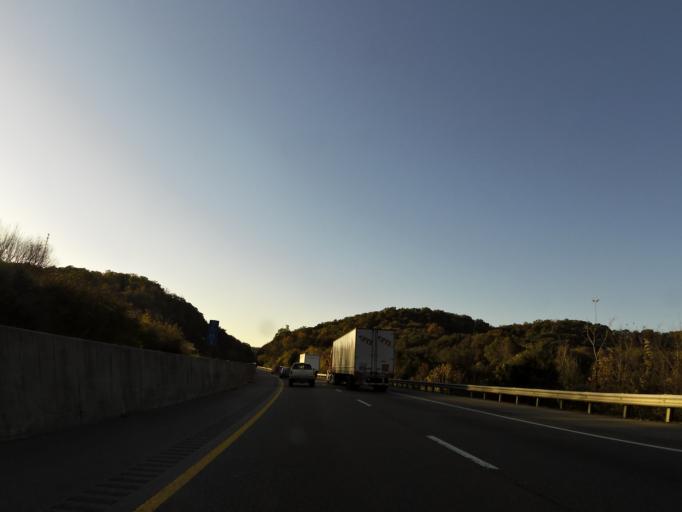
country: US
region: Tennessee
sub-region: Anderson County
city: Norris
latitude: 36.0947
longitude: -84.0136
